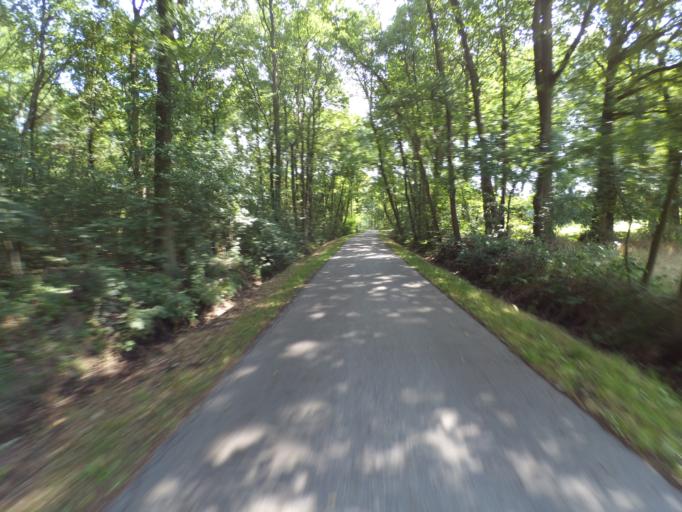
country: BE
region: Flanders
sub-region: Provincie Limburg
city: Kinrooi
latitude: 51.1218
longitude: 5.7072
